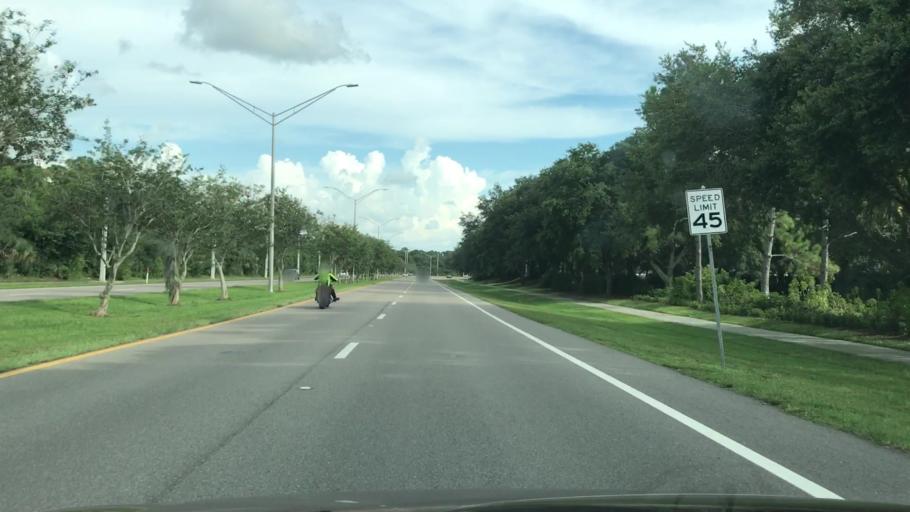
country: US
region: Florida
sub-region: Sarasota County
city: Venice Gardens
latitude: 27.0886
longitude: -82.3891
